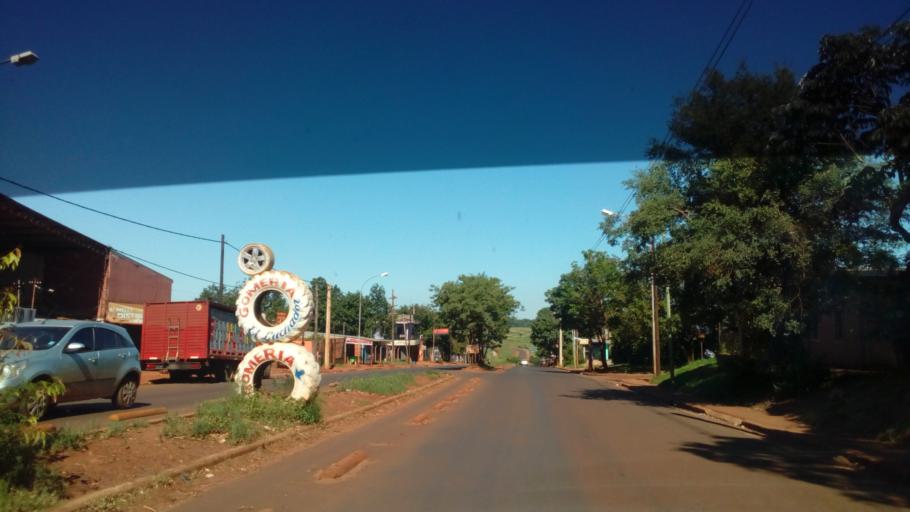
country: AR
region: Misiones
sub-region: Departamento de Capital
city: Posadas
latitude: -27.4280
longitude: -55.9125
